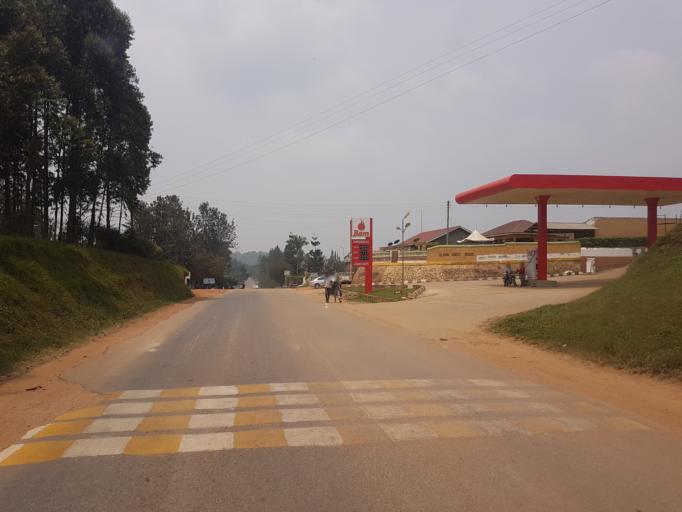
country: UG
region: Western Region
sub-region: Bushenyi District
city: Bushenyi
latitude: -0.5443
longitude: 30.2192
